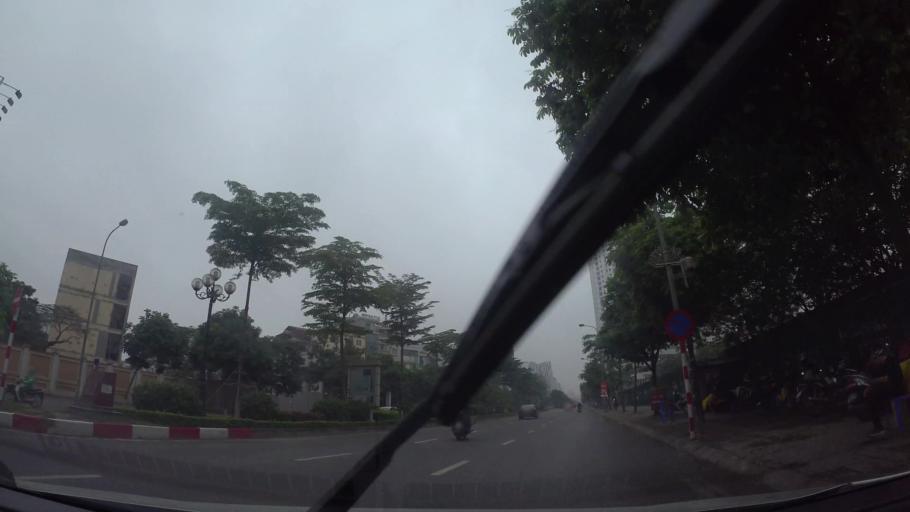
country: VN
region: Ha Noi
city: Cau Giay
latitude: 21.0226
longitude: 105.7902
